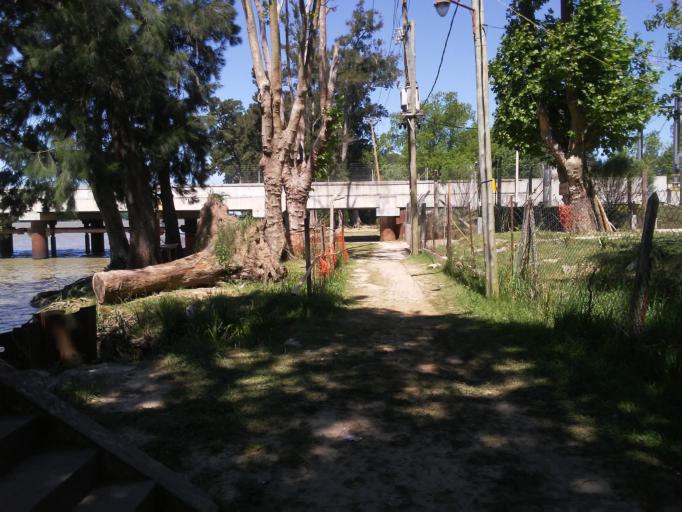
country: AR
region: Buenos Aires
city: Belen de Escobar
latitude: -34.2451
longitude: -58.7421
